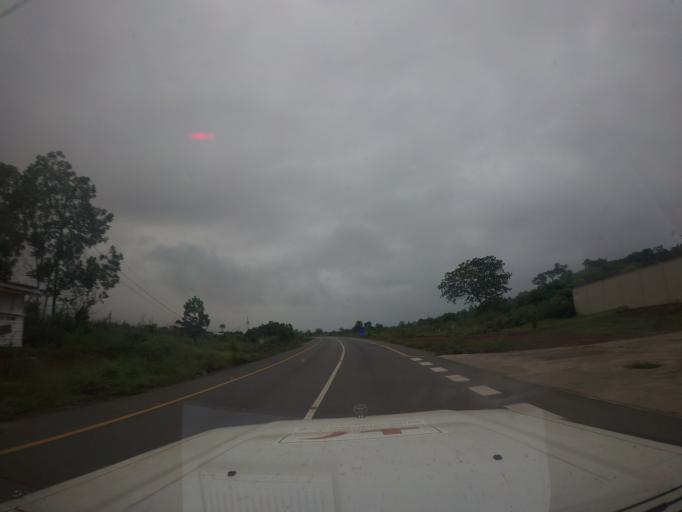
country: SL
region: Eastern Province
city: Hangha
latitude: 7.9240
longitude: -11.1517
